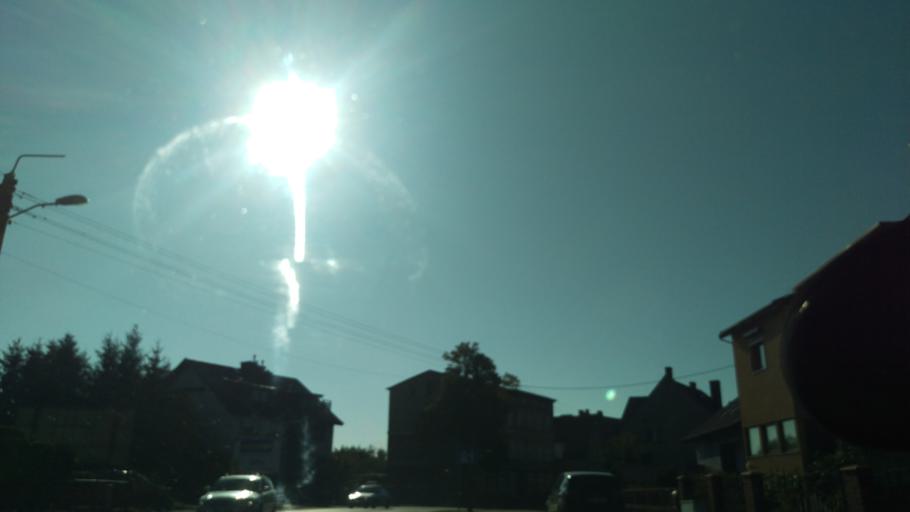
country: PL
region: West Pomeranian Voivodeship
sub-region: Szczecin
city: Szczecin
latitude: 53.3931
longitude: 14.6630
